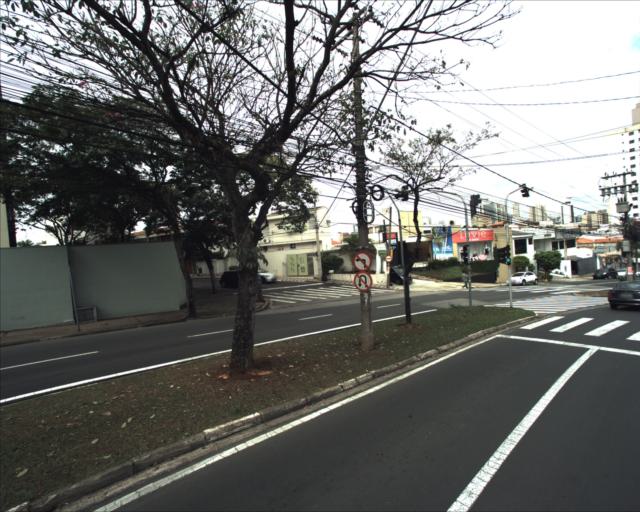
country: BR
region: Sao Paulo
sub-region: Sorocaba
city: Sorocaba
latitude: -23.5095
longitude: -47.4621
